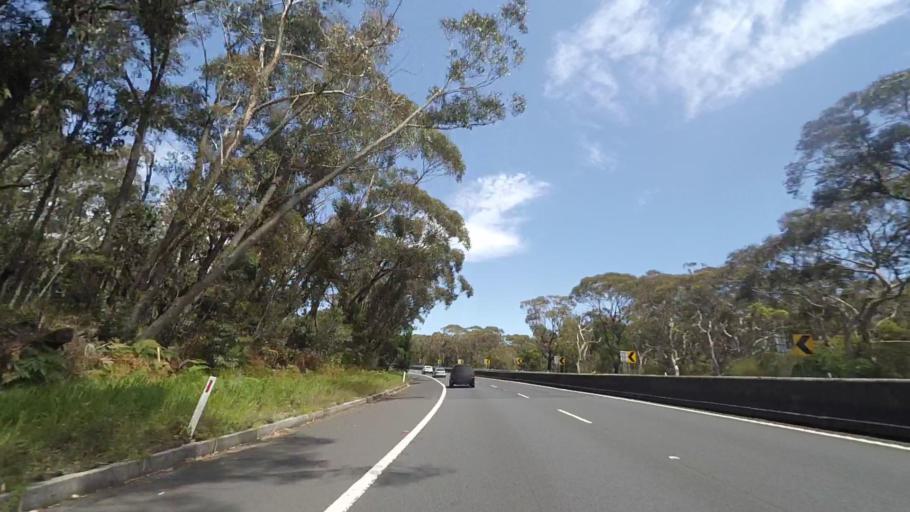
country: AU
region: New South Wales
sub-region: Wollongong
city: Mount Ousley
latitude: -34.3550
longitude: 150.8592
